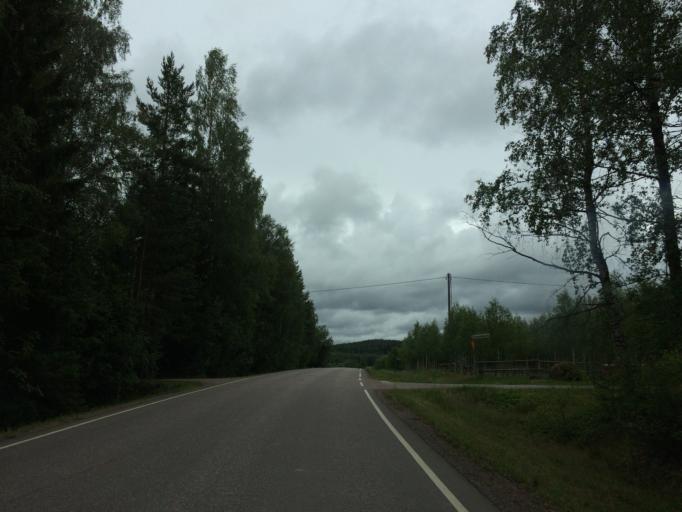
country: FI
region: Haeme
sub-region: Haemeenlinna
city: Janakkala
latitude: 60.8775
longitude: 24.5650
